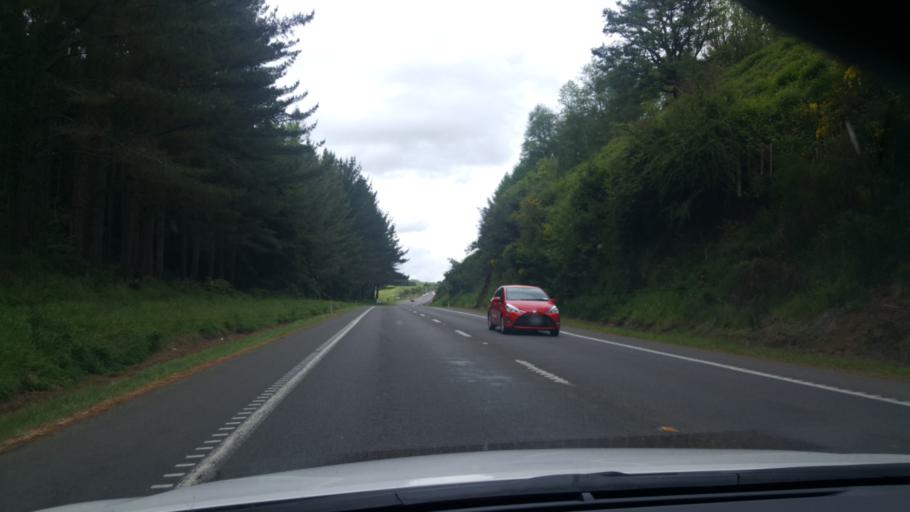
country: NZ
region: Bay of Plenty
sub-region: Rotorua District
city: Rotorua
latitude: -38.2426
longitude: 176.3074
